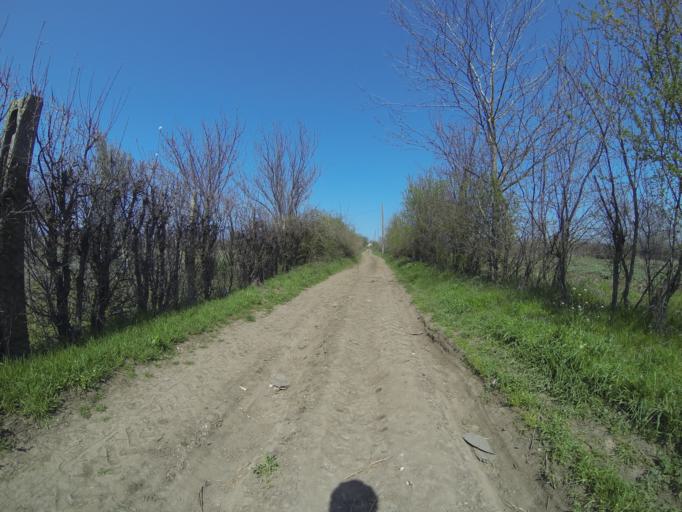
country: RO
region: Dolj
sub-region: Comuna Segarcea
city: Segarcea
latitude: 44.0955
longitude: 23.7295
